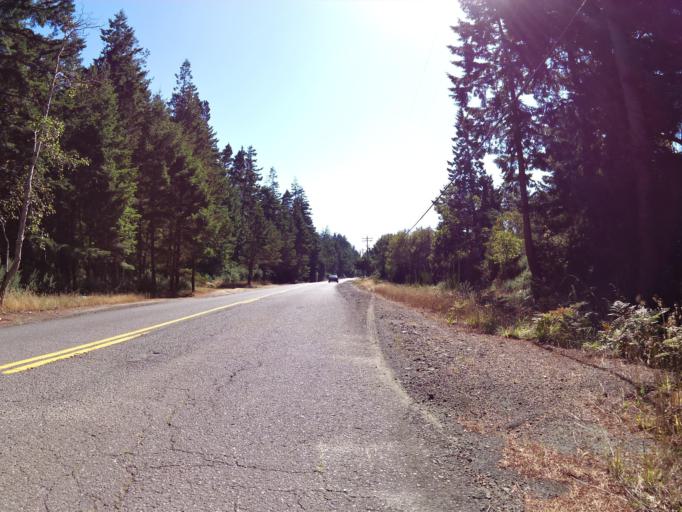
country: US
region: Oregon
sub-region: Coos County
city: Bandon
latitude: 43.1784
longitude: -124.3708
